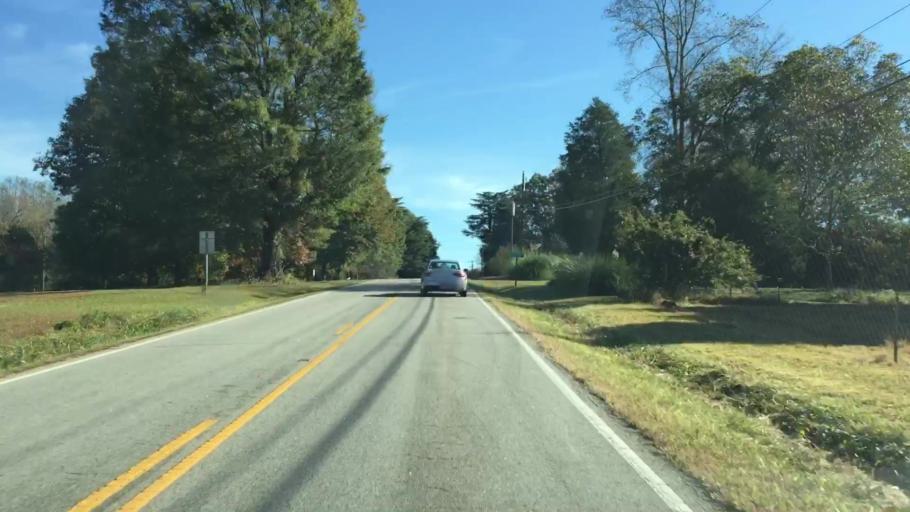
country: US
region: North Carolina
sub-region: Rowan County
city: China Grove
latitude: 35.6464
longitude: -80.6392
